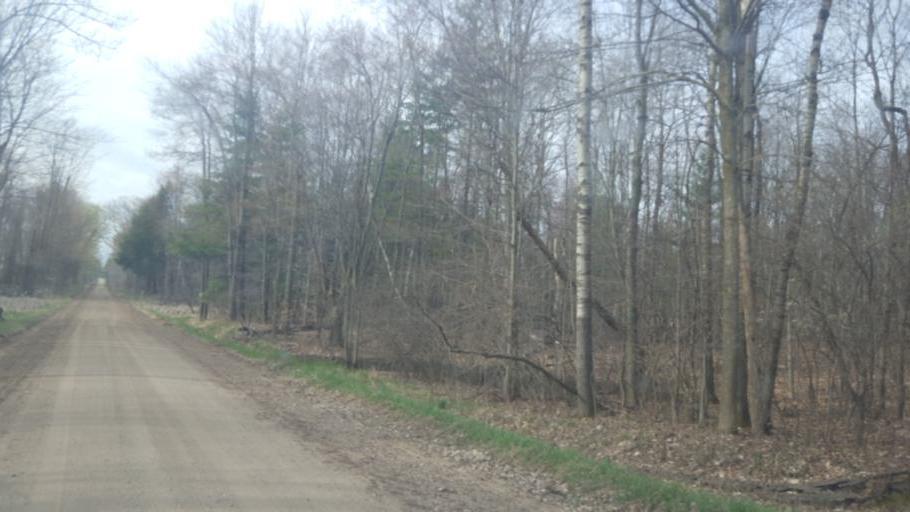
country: US
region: Michigan
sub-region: Isabella County
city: Lake Isabella
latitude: 43.5176
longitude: -84.9463
